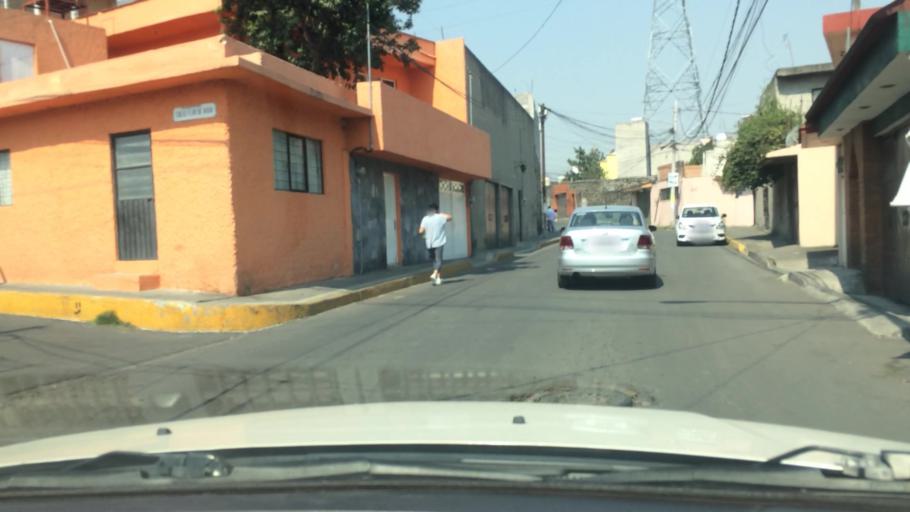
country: MX
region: Mexico City
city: Xochimilco
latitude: 19.2652
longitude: -99.1353
